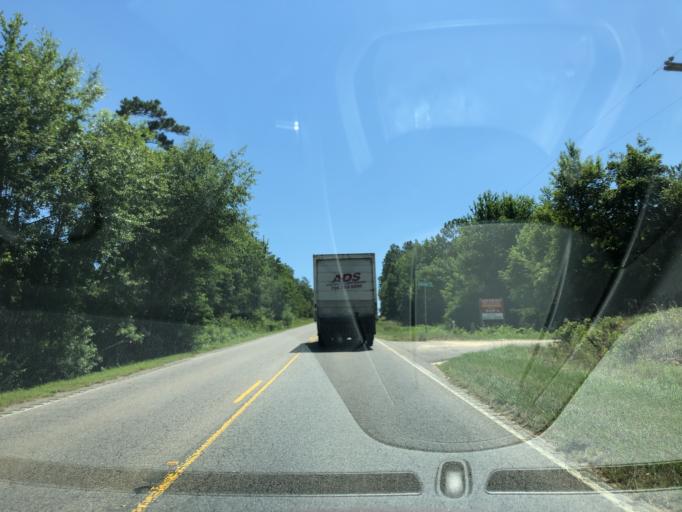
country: US
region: South Carolina
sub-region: Aiken County
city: Jackson
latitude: 33.4107
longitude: -81.8085
